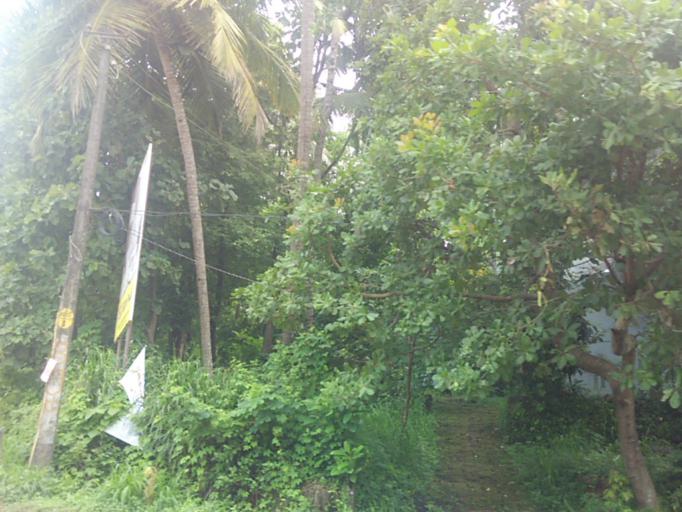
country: IN
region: Kerala
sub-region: Kozhikode
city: Kozhikode
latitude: 11.2825
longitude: 75.8041
